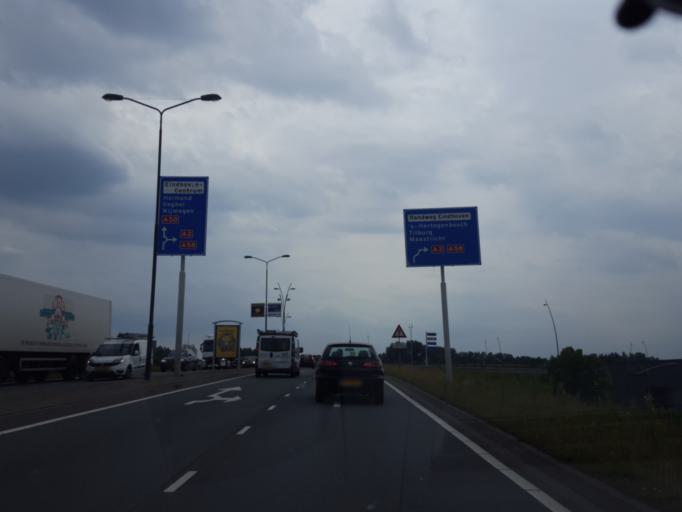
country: NL
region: North Brabant
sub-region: Gemeente Son en Breugel
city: Son
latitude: 51.4979
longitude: 5.4632
